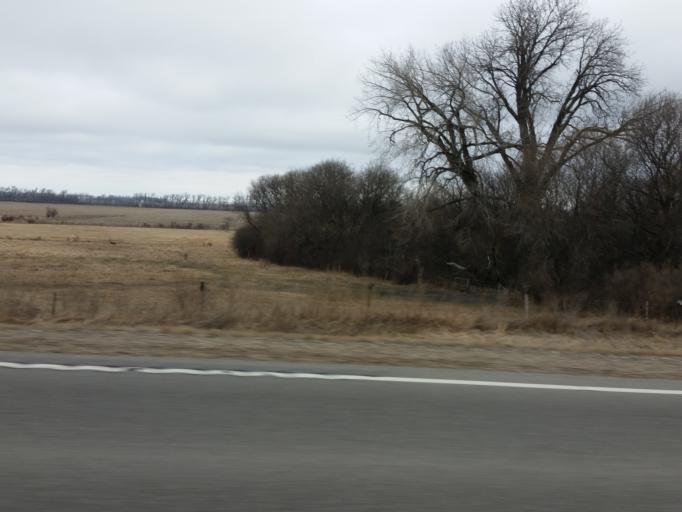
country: US
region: North Dakota
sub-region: Cass County
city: Horace
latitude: 46.6297
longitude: -97.1176
